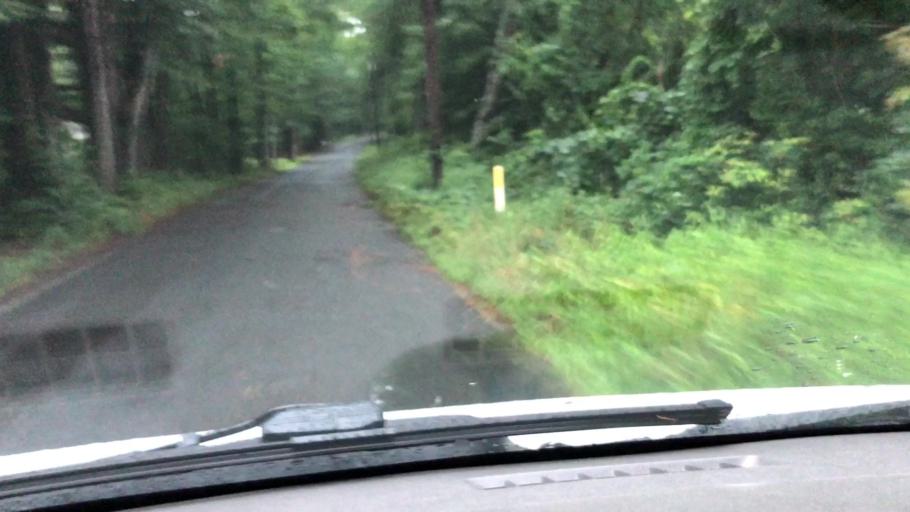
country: US
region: Massachusetts
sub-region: Hampshire County
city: Southampton
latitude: 42.2490
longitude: -72.7148
